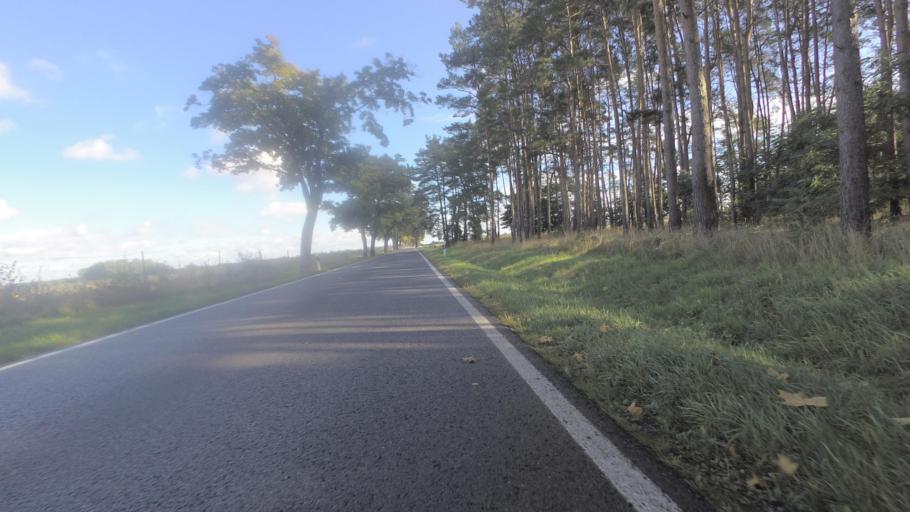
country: DE
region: Brandenburg
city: Juterbog
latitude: 51.8793
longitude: 13.0533
